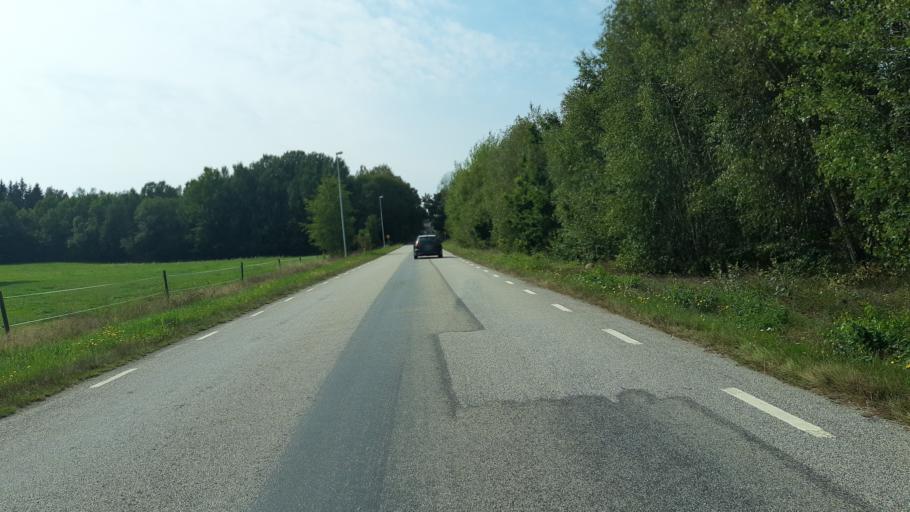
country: SE
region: Blekinge
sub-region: Ronneby Kommun
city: Kallinge
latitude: 56.2194
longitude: 15.3702
